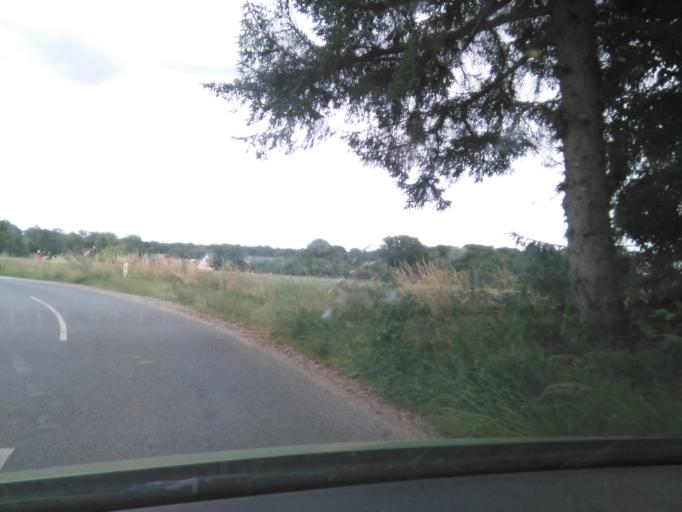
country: DK
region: Central Jutland
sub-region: Arhus Kommune
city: Marslet
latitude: 56.0297
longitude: 10.1512
